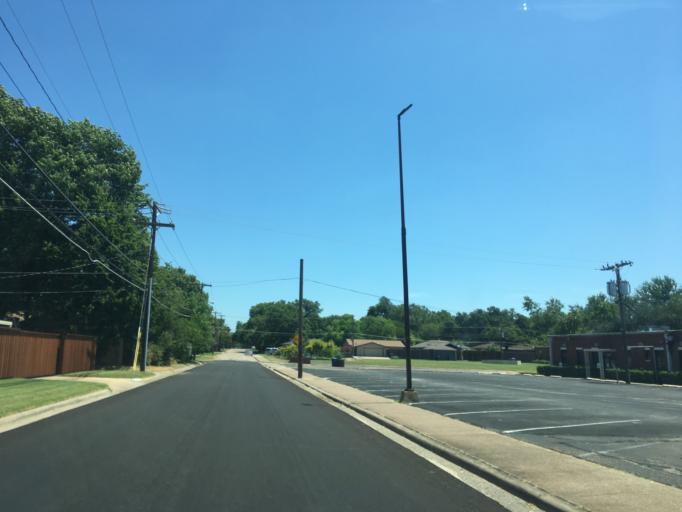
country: US
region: Texas
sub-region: Dallas County
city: Highland Park
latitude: 32.8506
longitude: -96.7091
